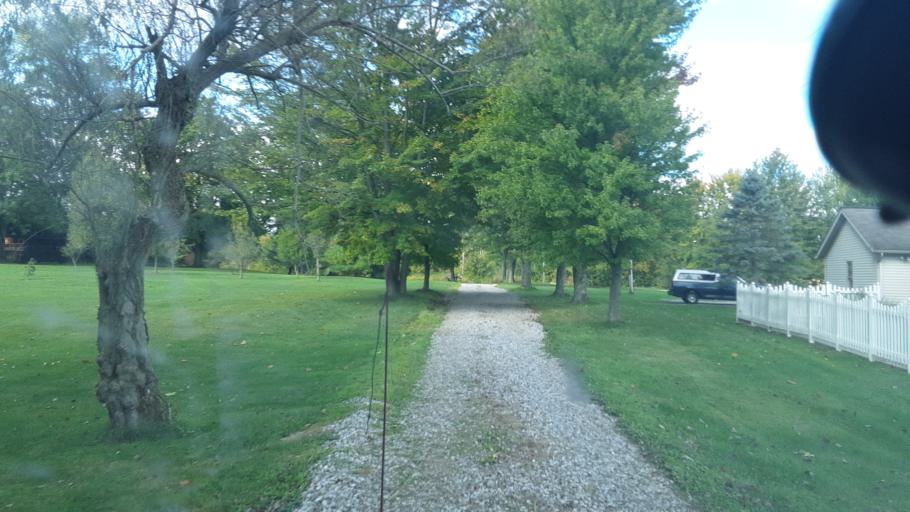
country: US
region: Ohio
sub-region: Knox County
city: Centerburg
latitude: 40.3006
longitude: -82.6160
